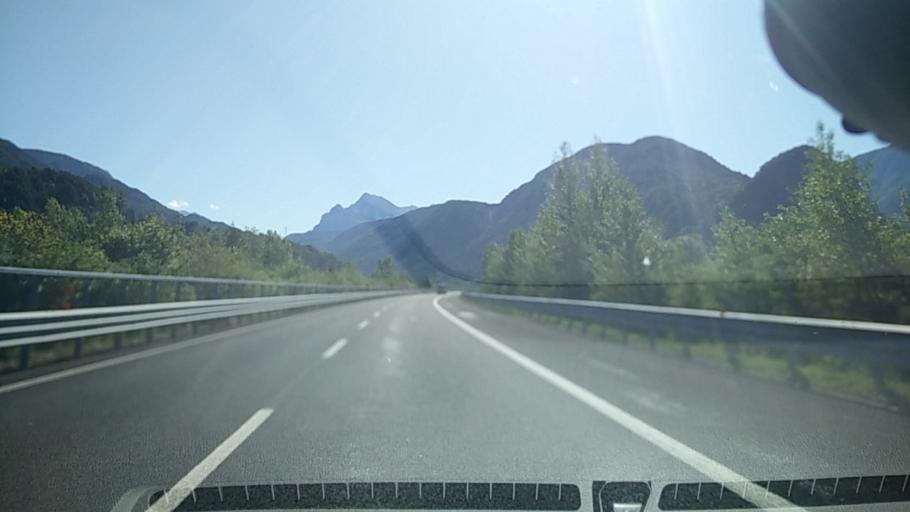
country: IT
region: Friuli Venezia Giulia
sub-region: Provincia di Udine
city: Resiutta
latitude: 46.3971
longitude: 13.2122
